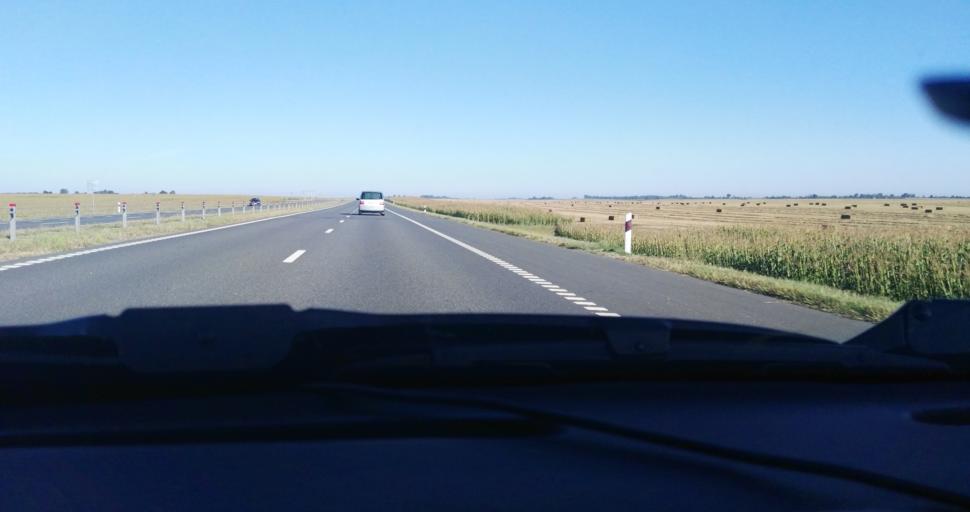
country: BY
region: Gomel
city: Buda-Kashalyova
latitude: 52.5226
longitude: 30.6229
